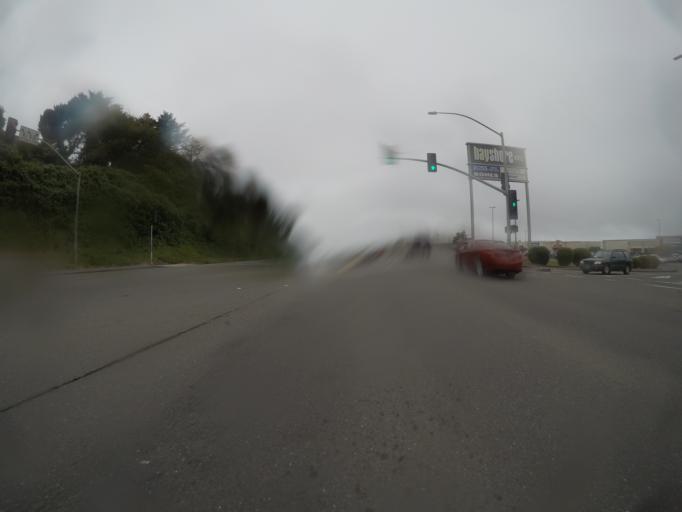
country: US
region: California
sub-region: Humboldt County
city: Bayview
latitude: 40.7790
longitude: -124.1876
